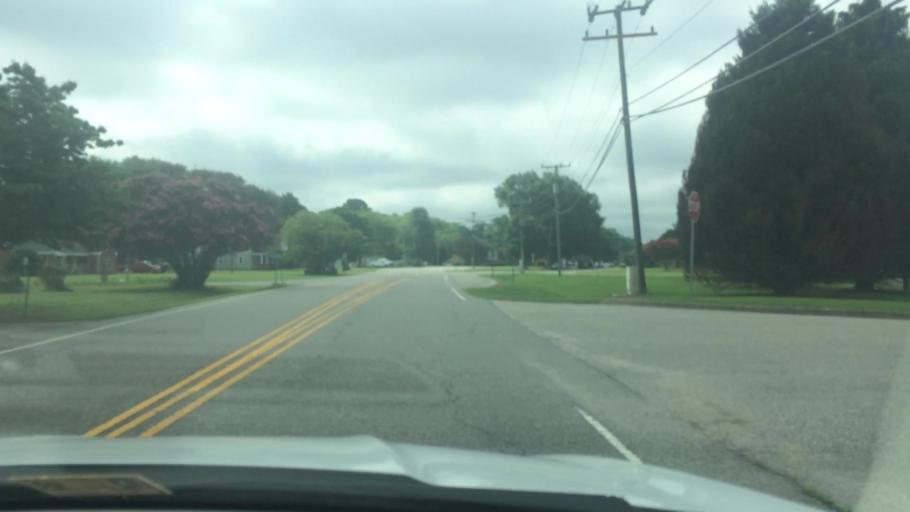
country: US
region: Virginia
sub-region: City of Poquoson
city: Poquoson
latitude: 37.1258
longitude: -76.4343
